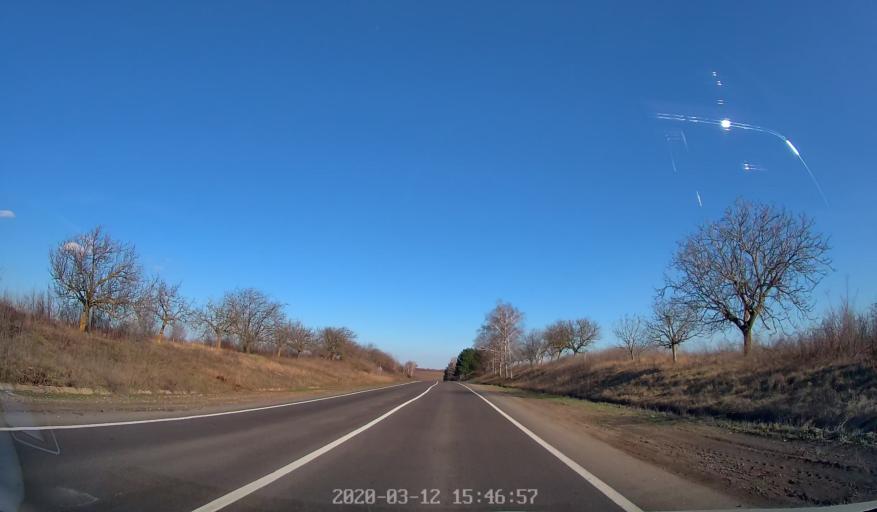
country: MD
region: Chisinau
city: Stauceni
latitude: 47.0975
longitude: 28.9017
